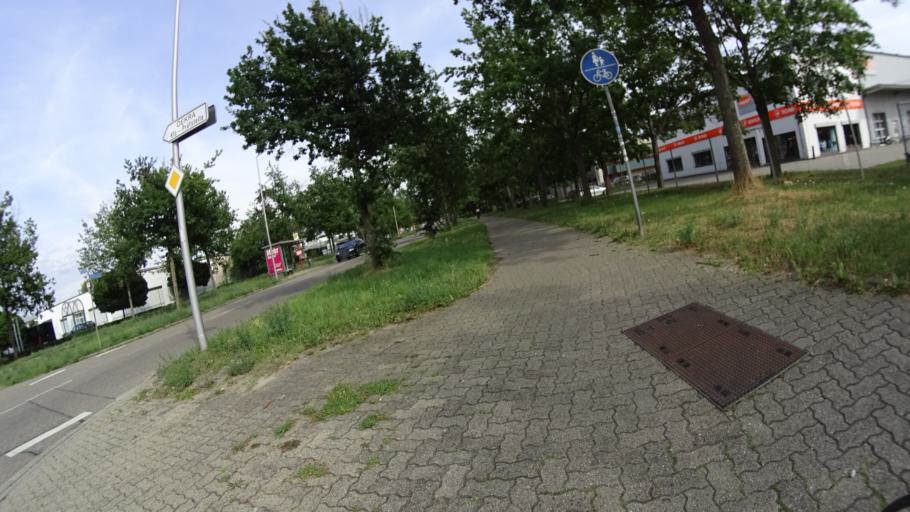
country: DE
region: Baden-Wuerttemberg
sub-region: Karlsruhe Region
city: Karlsruhe
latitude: 49.0328
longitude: 8.3550
